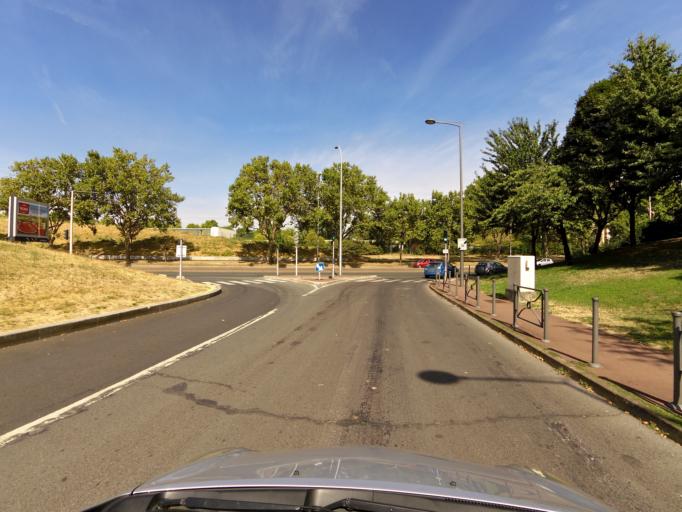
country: FR
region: Ile-de-France
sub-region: Departement du Val-de-Marne
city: Creteil
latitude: 48.7810
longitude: 2.4456
